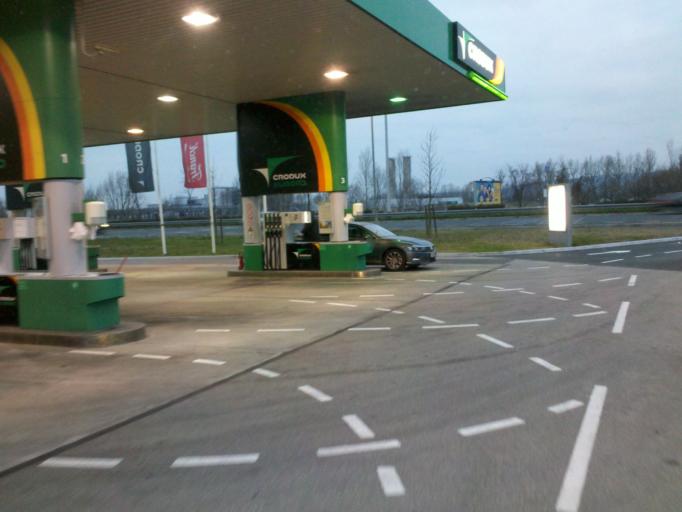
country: HR
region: Grad Zagreb
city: Zadvorsko
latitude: 45.7679
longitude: 15.9286
